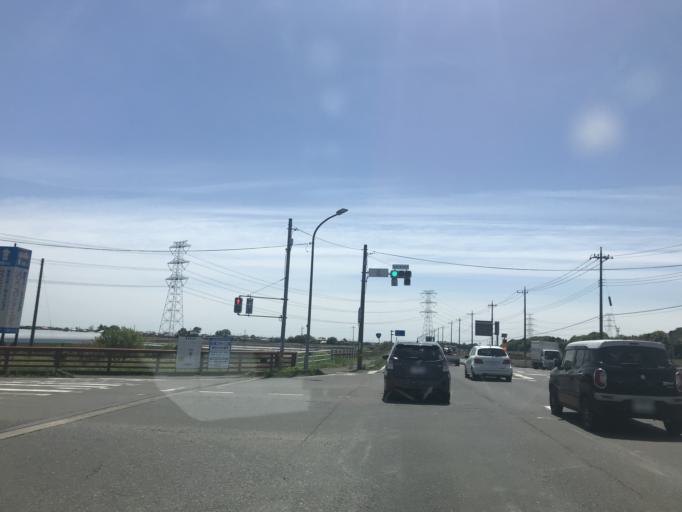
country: JP
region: Ibaraki
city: Shimodate
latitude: 36.2493
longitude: 139.9833
